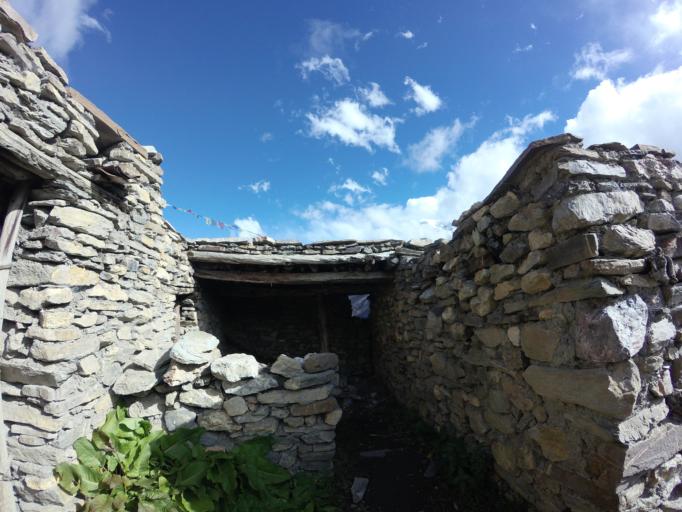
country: NP
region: Western Region
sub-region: Gandaki Zone
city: Nawal
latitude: 28.6767
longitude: 83.9719
